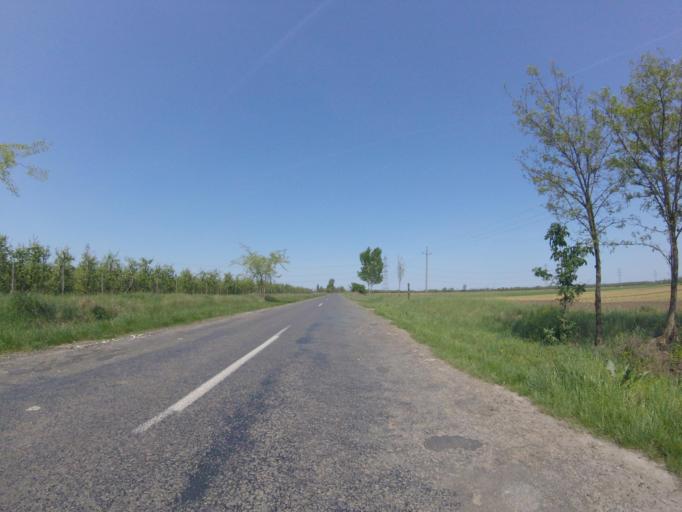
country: HU
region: Pest
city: Nyaregyhaza
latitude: 47.2499
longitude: 19.5215
